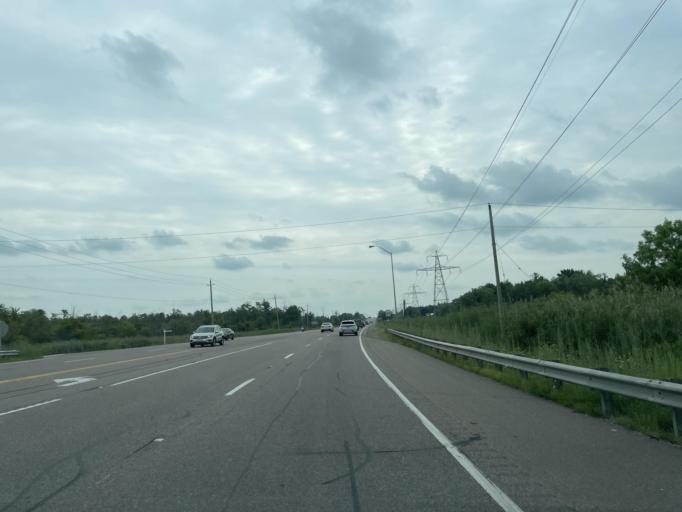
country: CA
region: Ontario
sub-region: Halton
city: Milton
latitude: 43.4088
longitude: -80.0485
